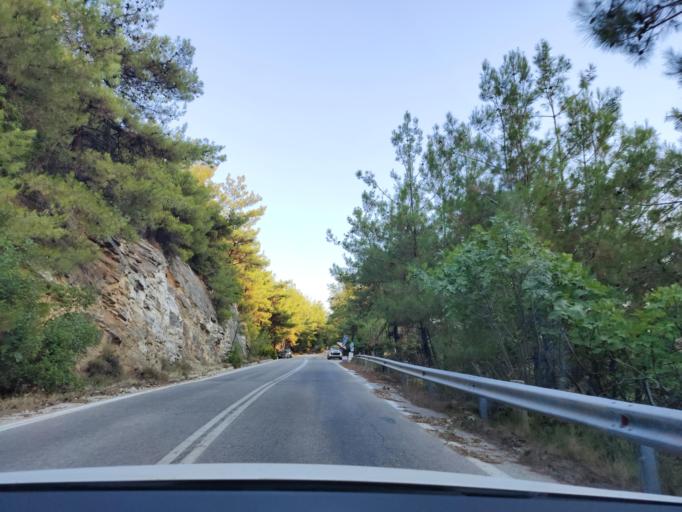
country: GR
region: East Macedonia and Thrace
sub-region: Nomos Kavalas
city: Potamia
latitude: 40.6280
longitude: 24.7656
